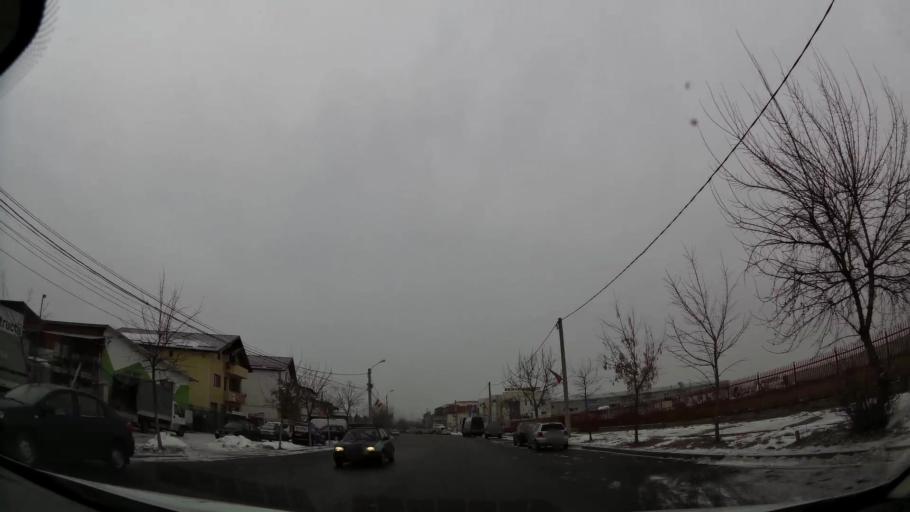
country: RO
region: Dambovita
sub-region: Municipiul Targoviste
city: Targoviste
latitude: 44.9365
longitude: 25.4414
